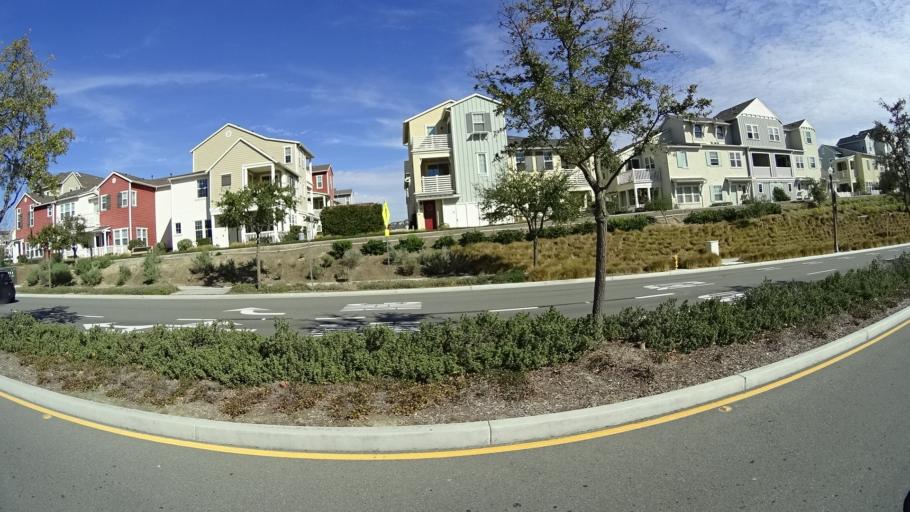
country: US
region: California
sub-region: Orange County
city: Ladera Ranch
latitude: 33.5332
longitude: -117.6009
